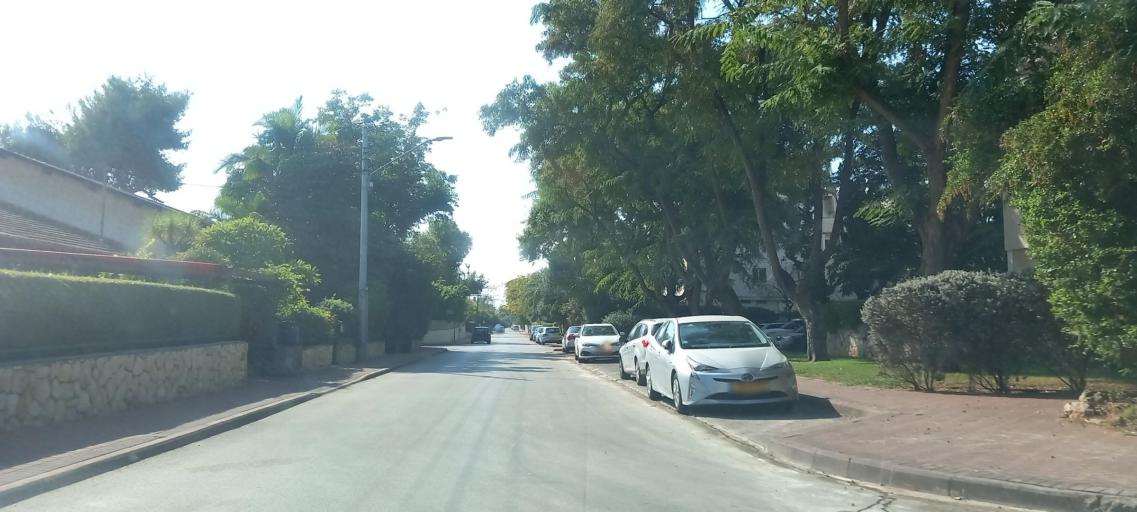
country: IL
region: Tel Aviv
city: Or Yehuda
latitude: 32.0471
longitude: 34.8384
